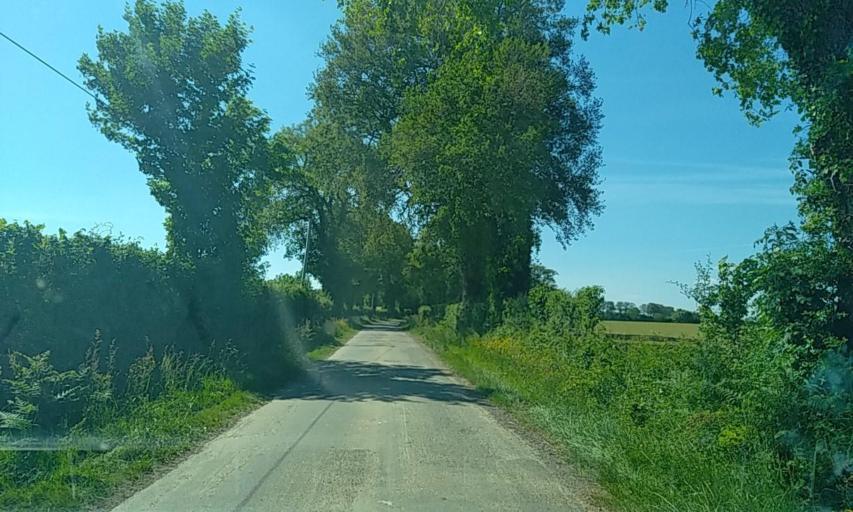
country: FR
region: Poitou-Charentes
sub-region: Departement des Deux-Sevres
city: Boisme
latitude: 46.7796
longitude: -0.4564
